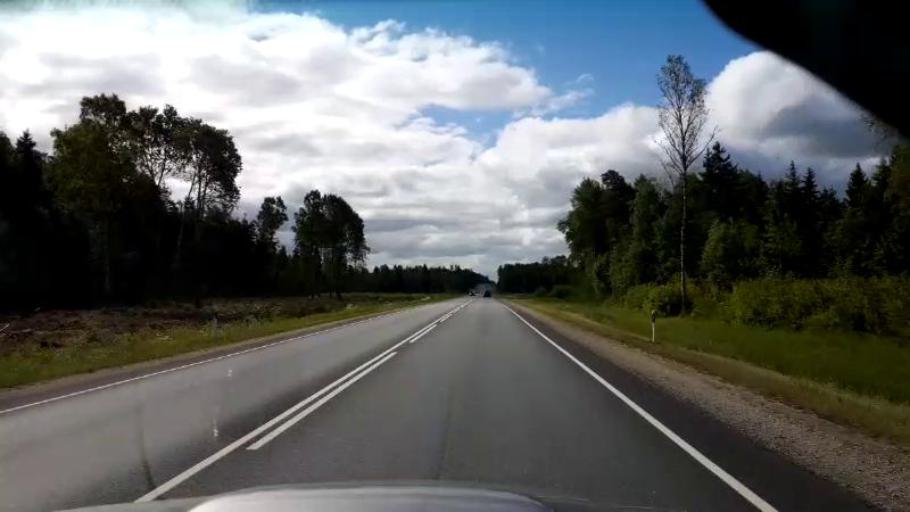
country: EE
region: Raplamaa
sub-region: Maerjamaa vald
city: Marjamaa
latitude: 59.0274
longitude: 24.4467
